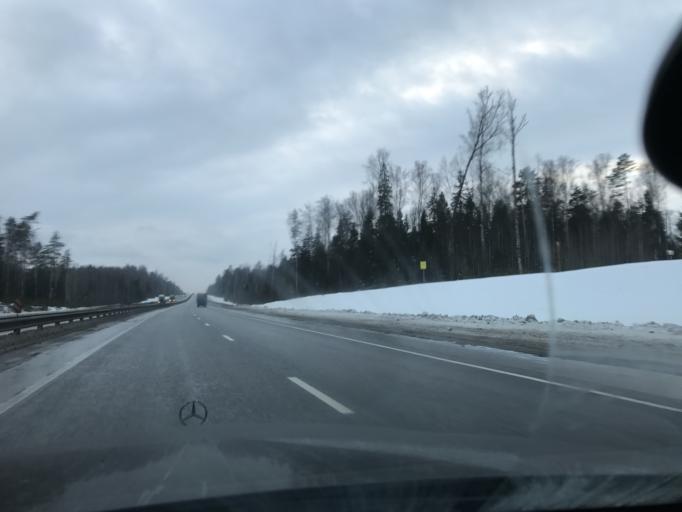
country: RU
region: Vladimir
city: Sudogda
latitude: 56.1465
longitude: 40.9112
